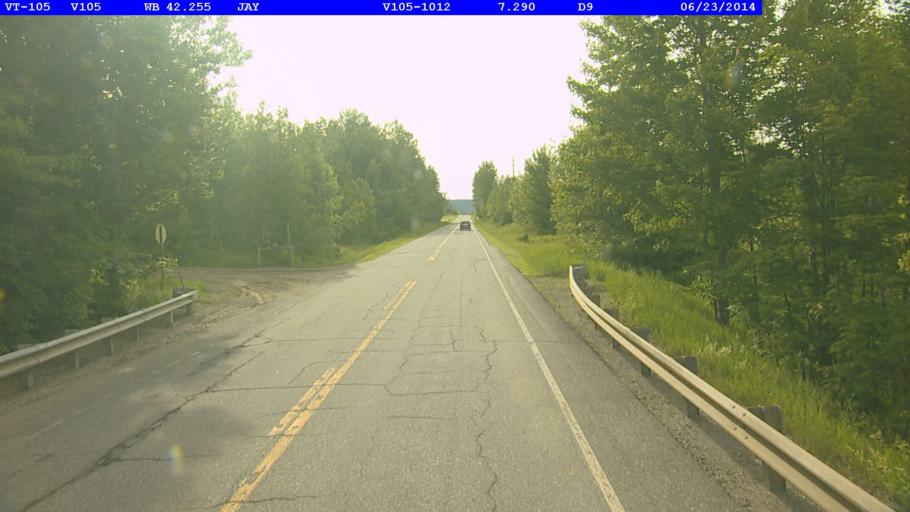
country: CA
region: Quebec
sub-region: Monteregie
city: Sutton
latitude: 44.9685
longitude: -72.4429
